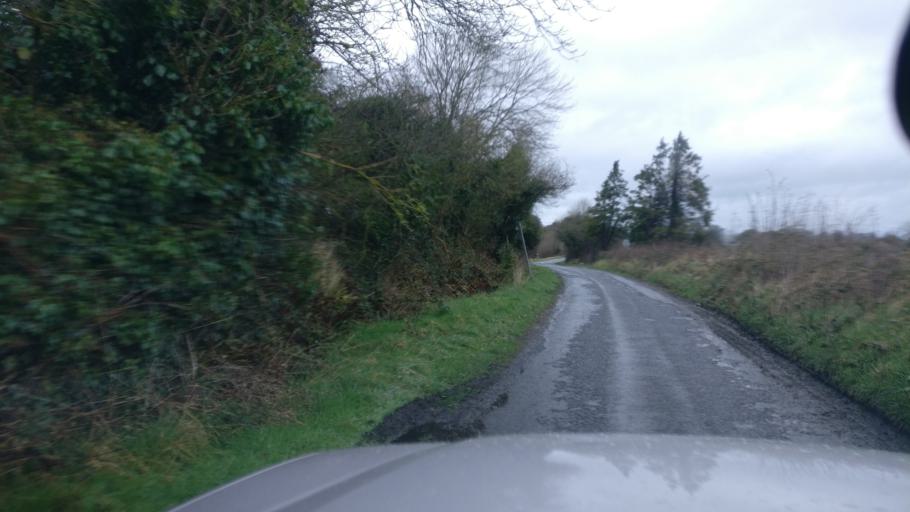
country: IE
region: Connaught
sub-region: County Galway
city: Ballinasloe
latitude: 53.2553
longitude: -8.3552
